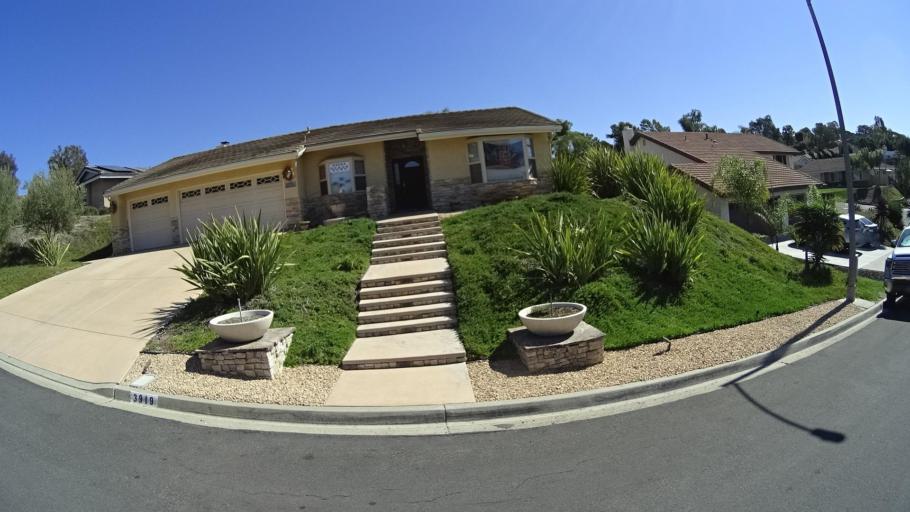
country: US
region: California
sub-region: San Diego County
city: Bonita
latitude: 32.6673
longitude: -117.0023
